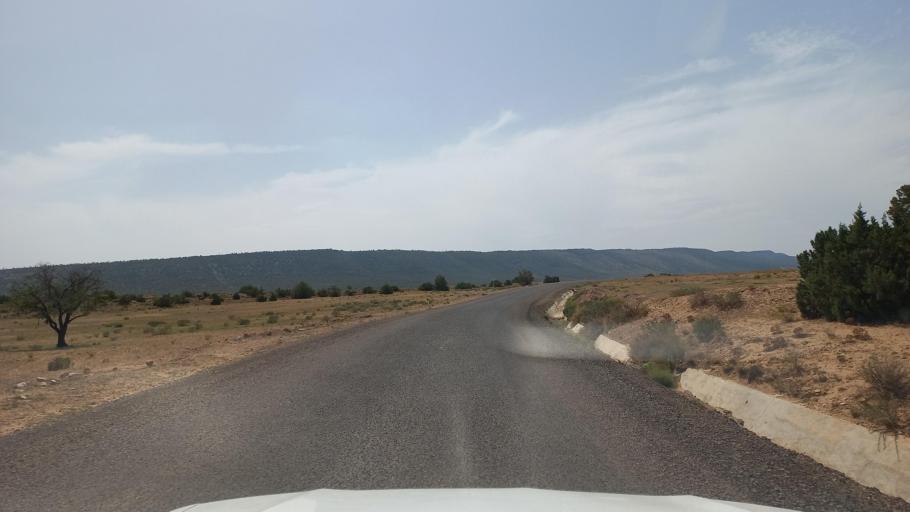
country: TN
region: Al Qasrayn
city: Sbiba
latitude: 35.3913
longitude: 8.9492
